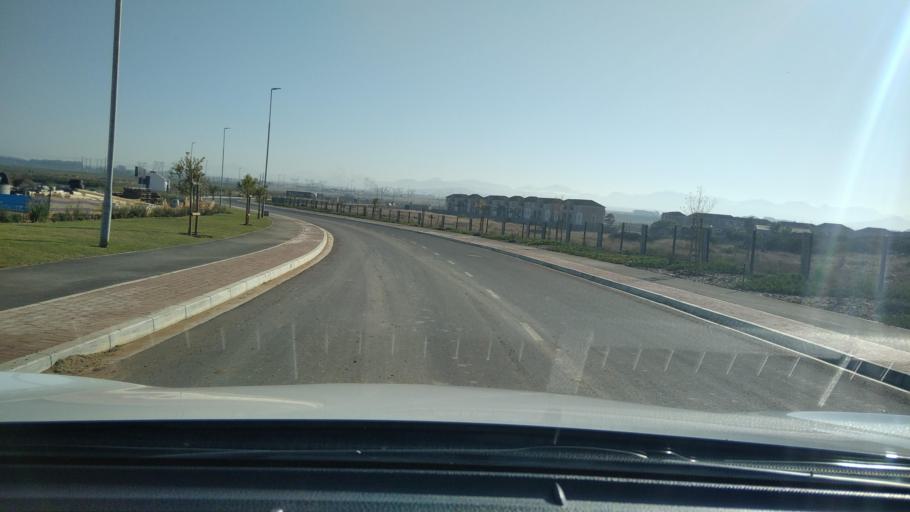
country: ZA
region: Western Cape
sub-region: City of Cape Town
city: Kraaifontein
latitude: -33.8114
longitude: 18.6904
